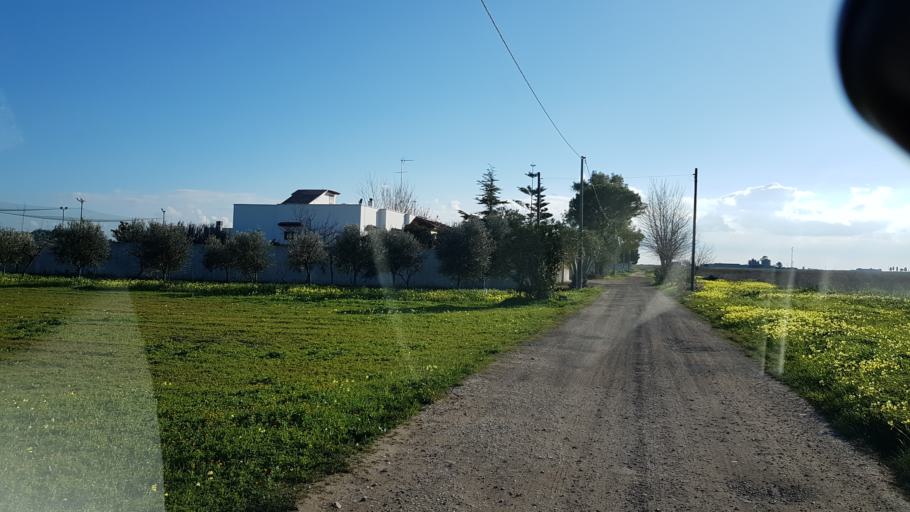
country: IT
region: Apulia
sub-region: Provincia di Brindisi
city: Tuturano
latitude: 40.5424
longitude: 17.9587
